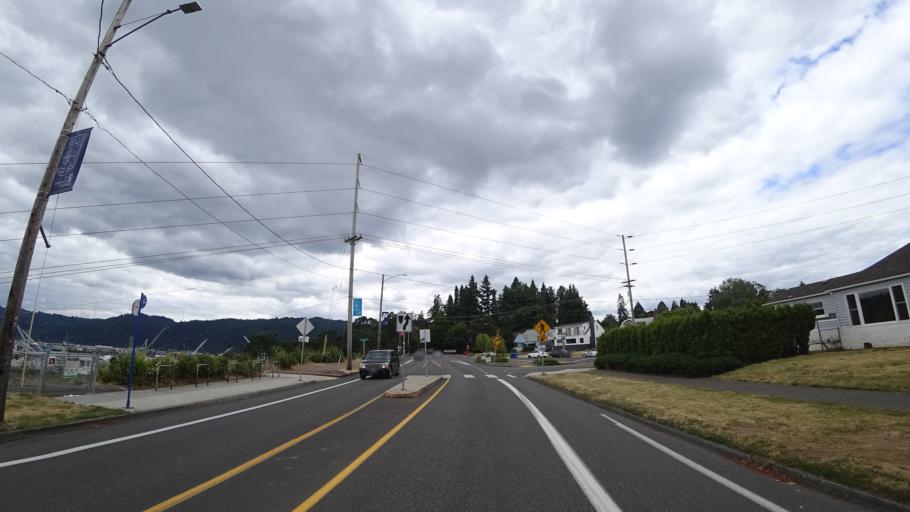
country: US
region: Oregon
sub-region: Multnomah County
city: Portland
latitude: 45.5741
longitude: -122.7200
